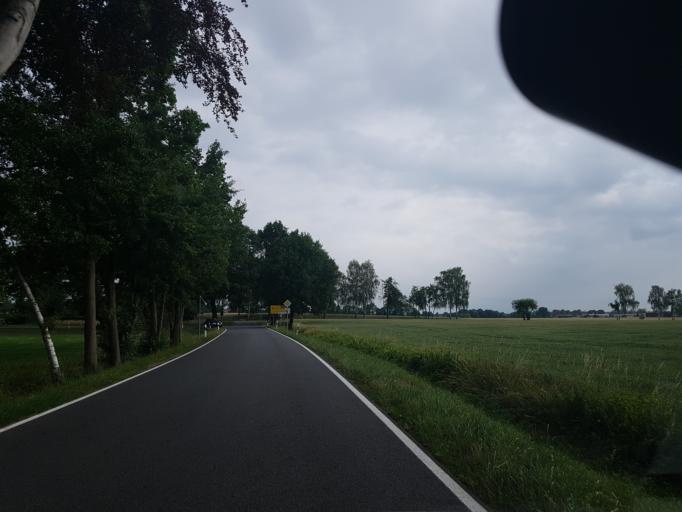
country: DE
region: Brandenburg
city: Sonnewalde
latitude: 51.6998
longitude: 13.6219
